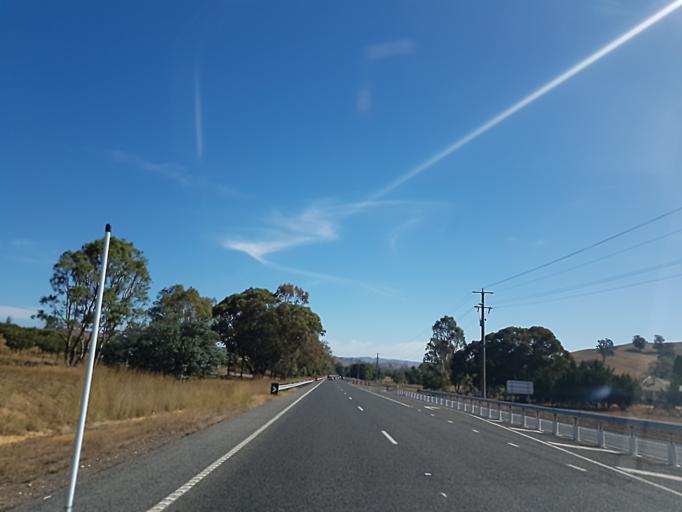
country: AU
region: Victoria
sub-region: Murrindindi
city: Alexandra
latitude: -37.2032
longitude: 145.4639
